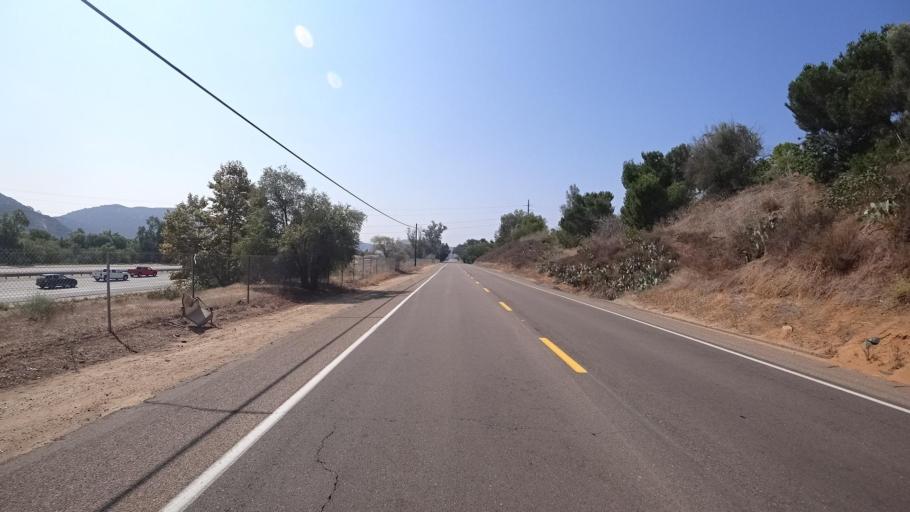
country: US
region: California
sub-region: San Diego County
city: Rainbow
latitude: 33.3483
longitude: -117.1597
